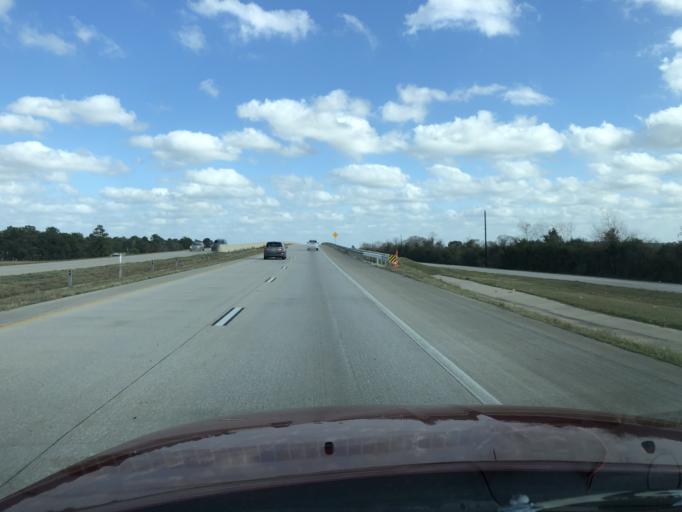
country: US
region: Texas
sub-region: Harris County
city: Cypress
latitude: 30.0498
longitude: -95.6836
